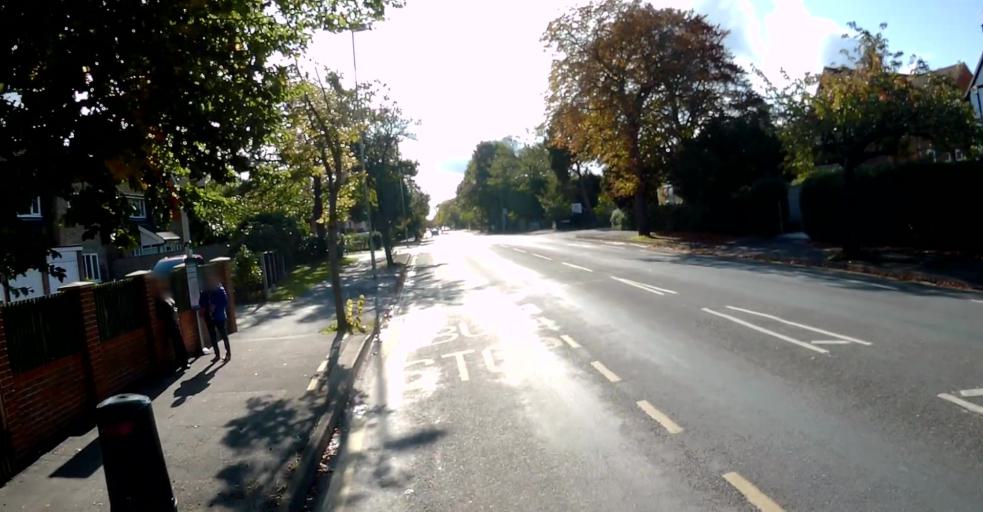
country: GB
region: England
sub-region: Hampshire
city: Farnborough
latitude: 51.2844
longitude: -0.7509
